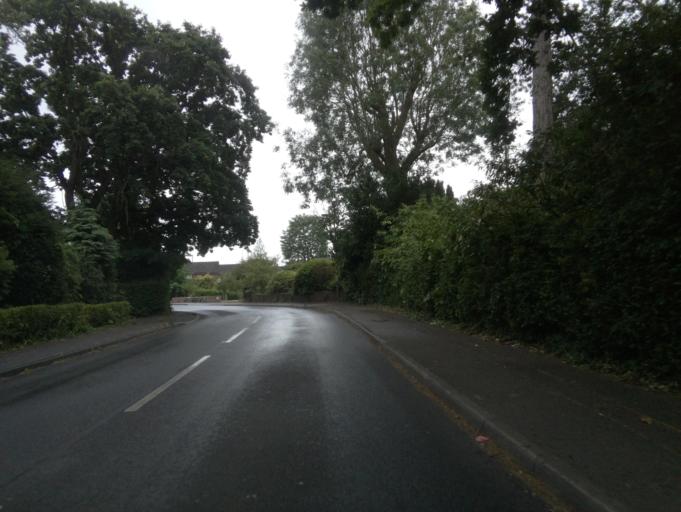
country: GB
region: England
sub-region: Surrey
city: Redhill
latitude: 51.2423
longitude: -0.1890
